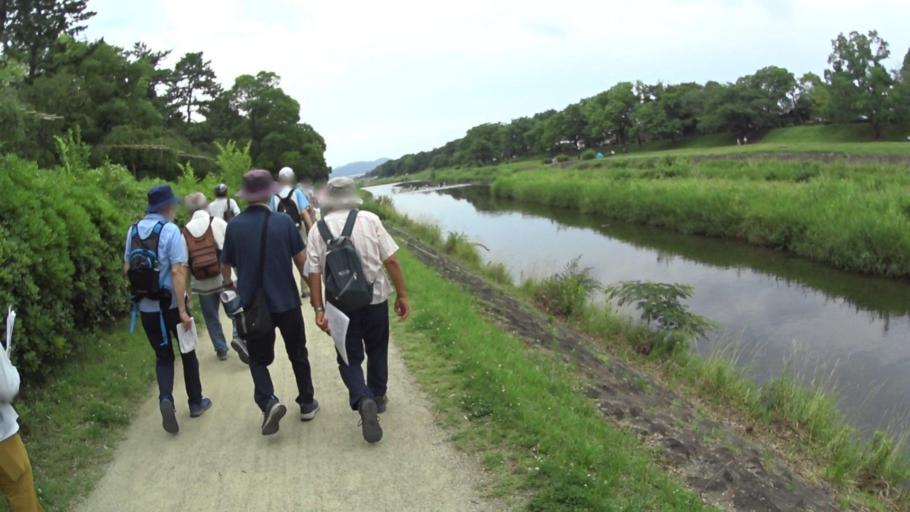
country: JP
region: Kyoto
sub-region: Kyoto-shi
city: Kamigyo-ku
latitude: 35.0464
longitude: 135.7620
